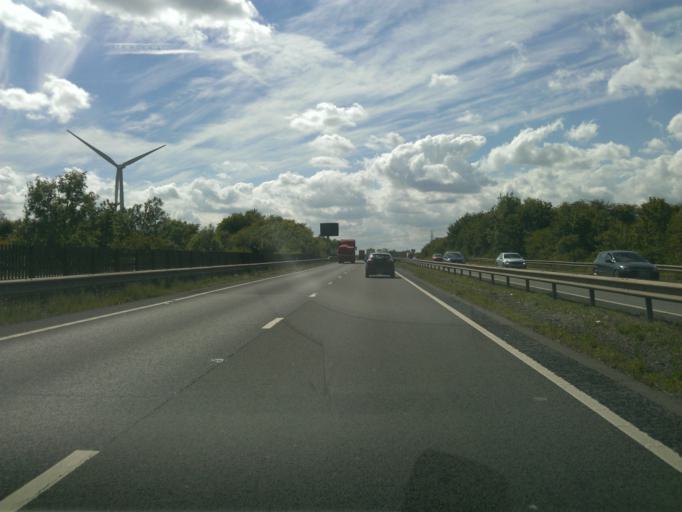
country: GB
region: England
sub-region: Northamptonshire
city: Burton Latimer
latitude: 52.3803
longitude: -0.6463
